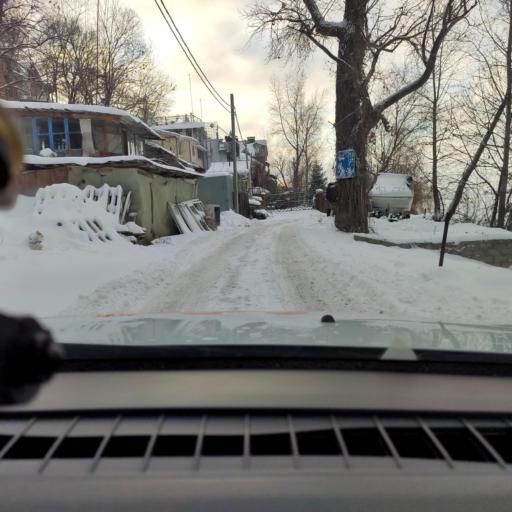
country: RU
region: Samara
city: Samara
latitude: 53.2847
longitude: 50.1900
